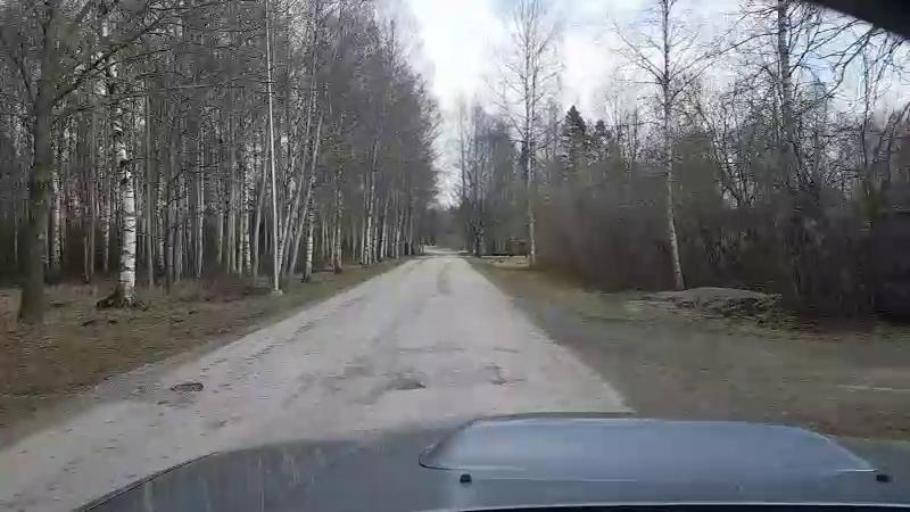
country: EE
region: Jaervamaa
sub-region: Paide linn
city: Paide
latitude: 58.8850
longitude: 25.5296
